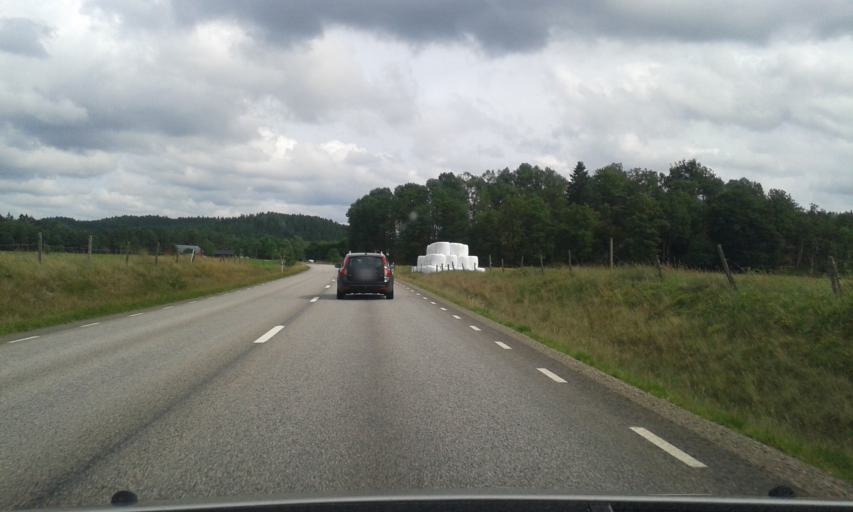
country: SE
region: Vaestra Goetaland
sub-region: Marks Kommun
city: Horred
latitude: 57.1508
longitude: 12.6801
